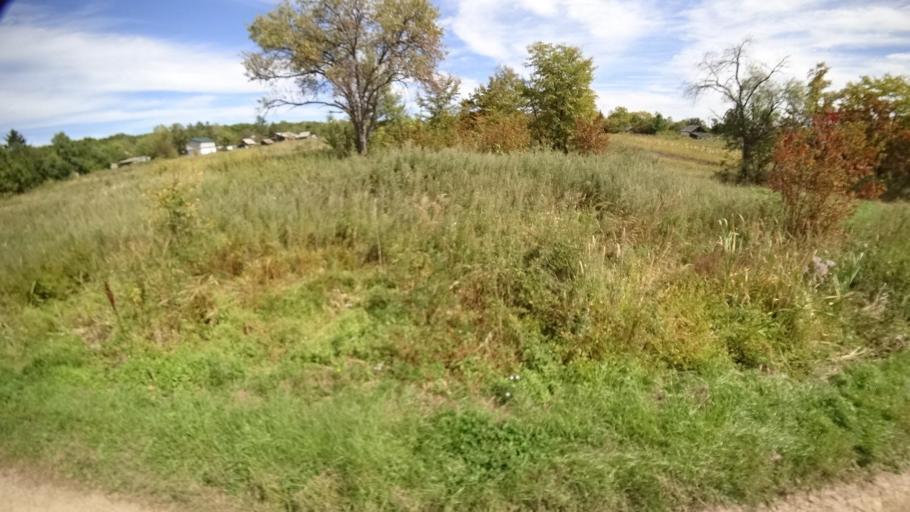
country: RU
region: Primorskiy
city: Yakovlevka
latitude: 44.6467
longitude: 133.5881
